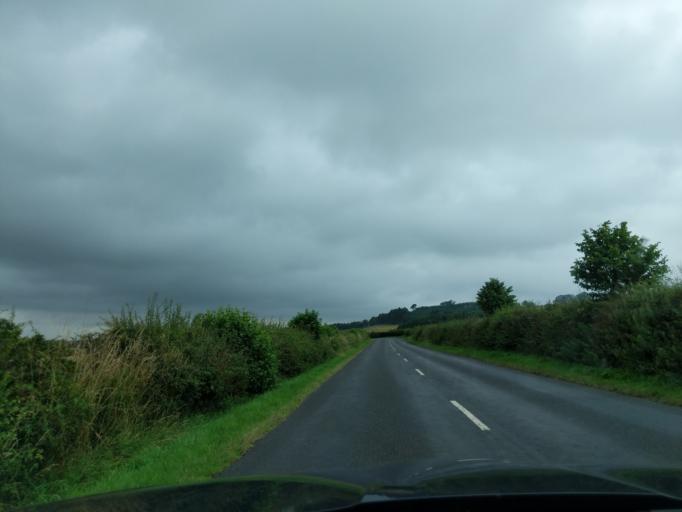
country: GB
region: England
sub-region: Northumberland
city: Ford
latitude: 55.6368
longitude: -2.1023
